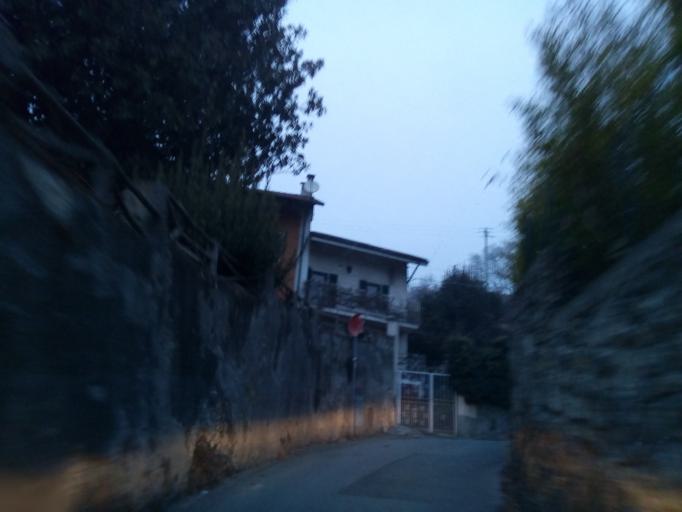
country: IT
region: Piedmont
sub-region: Provincia di Torino
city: Ivrea
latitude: 45.4756
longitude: 7.8750
